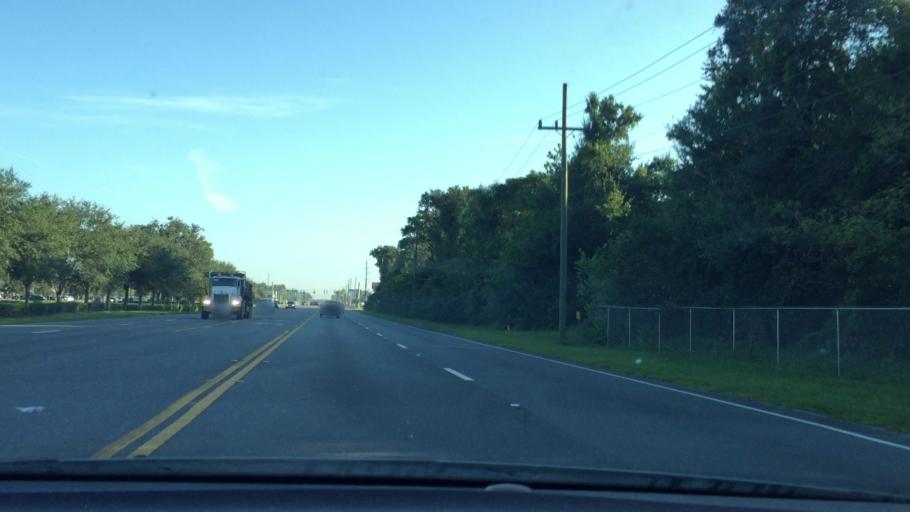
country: US
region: Florida
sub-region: Osceola County
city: Kissimmee
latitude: 28.3154
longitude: -81.4037
